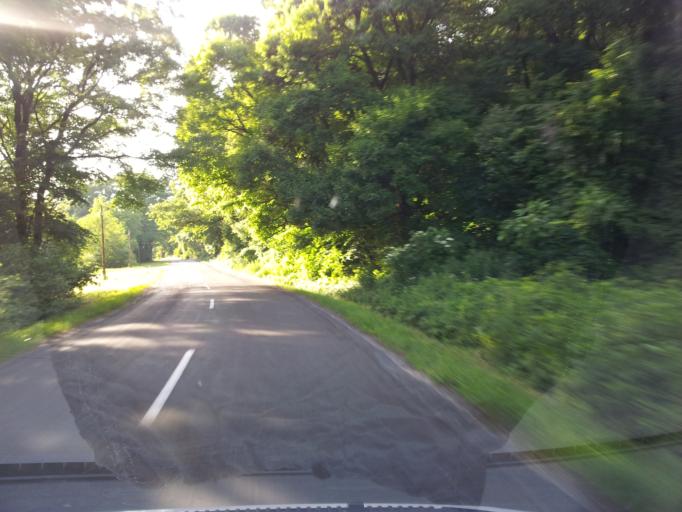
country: HU
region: Komarom-Esztergom
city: Kesztolc
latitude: 47.7437
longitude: 18.8065
